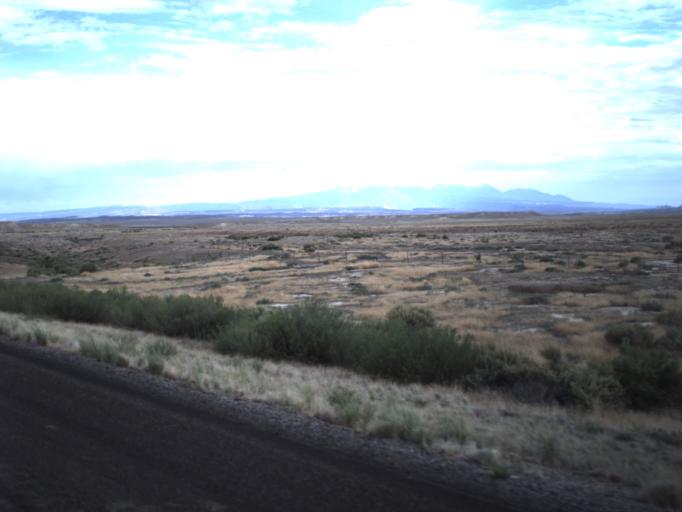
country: US
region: Utah
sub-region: Grand County
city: Moab
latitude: 38.9454
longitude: -109.6521
